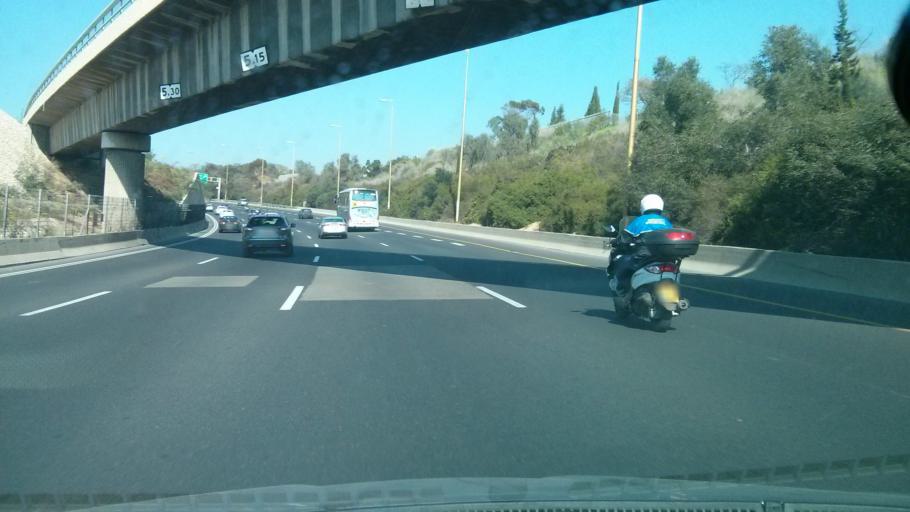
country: IL
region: Tel Aviv
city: Ramat Gan
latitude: 32.1124
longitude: 34.8106
